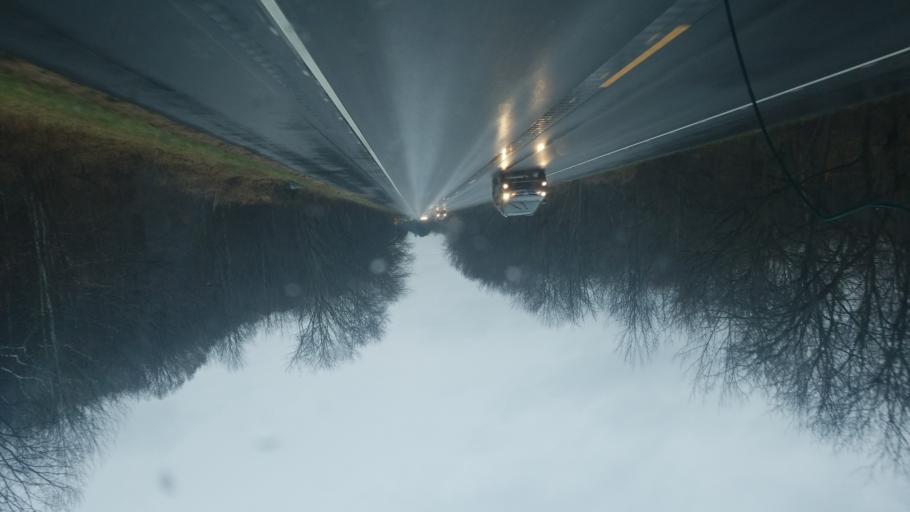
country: US
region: Indiana
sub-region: Brown County
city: Nashville
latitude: 39.1967
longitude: -86.2104
